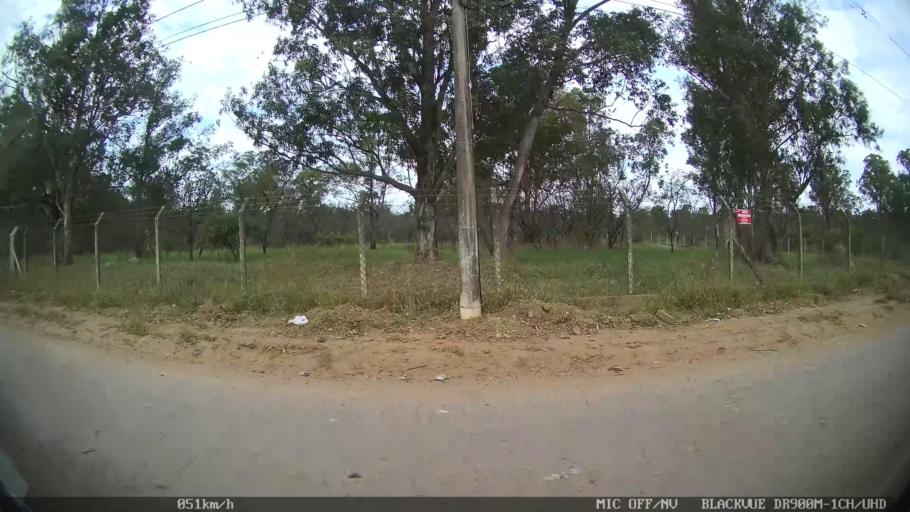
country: BR
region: Sao Paulo
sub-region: Paulinia
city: Paulinia
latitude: -22.7246
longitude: -47.1639
